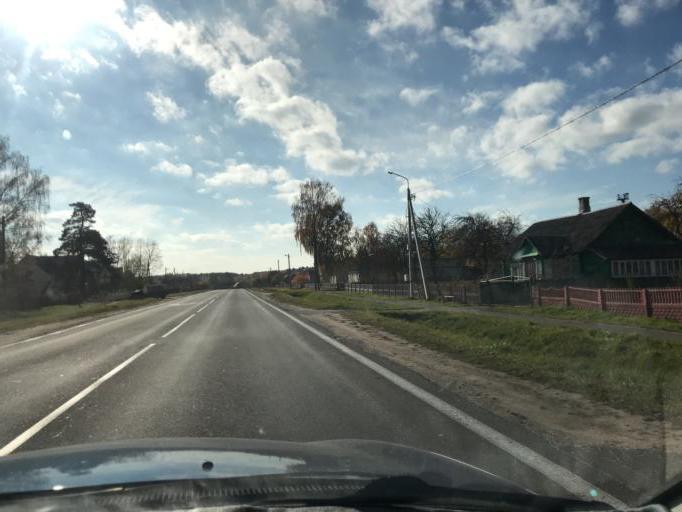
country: LT
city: Salcininkai
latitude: 54.2438
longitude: 25.3552
